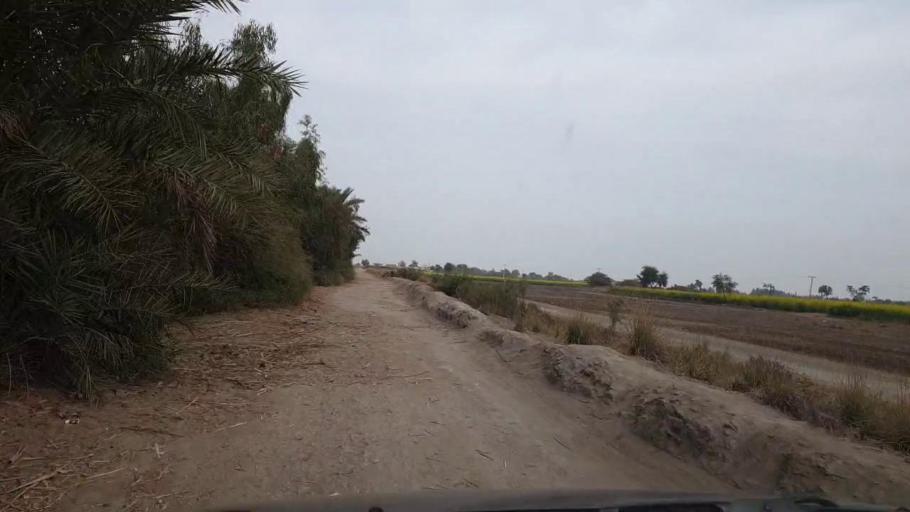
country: PK
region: Sindh
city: Sanghar
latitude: 26.1140
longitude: 68.8963
